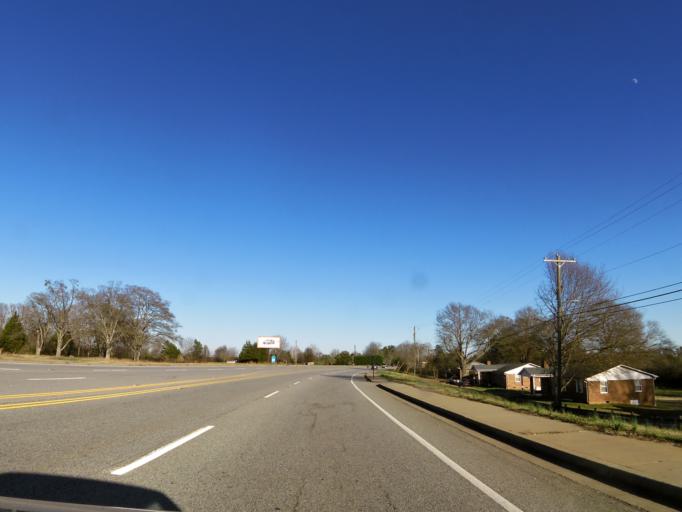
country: US
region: South Carolina
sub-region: Spartanburg County
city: Wellford
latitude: 34.8893
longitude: -82.0587
